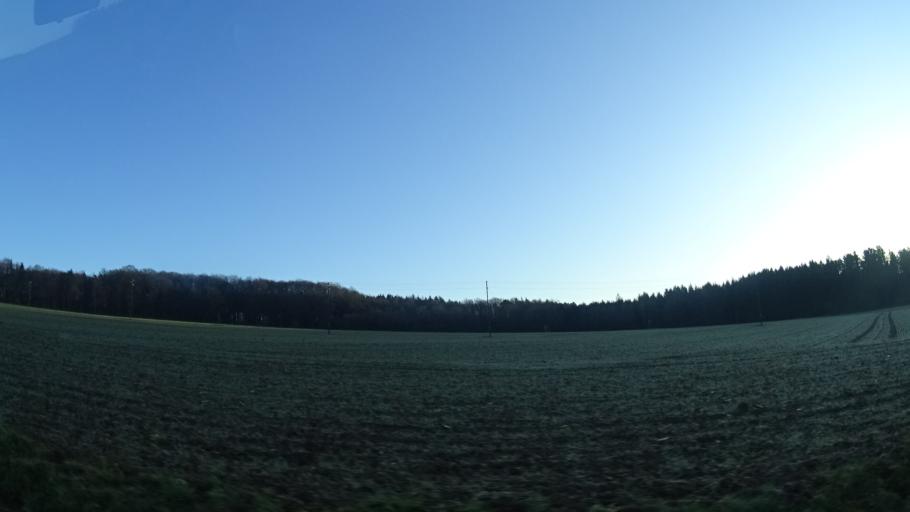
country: DE
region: Bavaria
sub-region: Regierungsbezirk Unterfranken
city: Miltenberg
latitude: 49.6697
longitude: 9.2840
